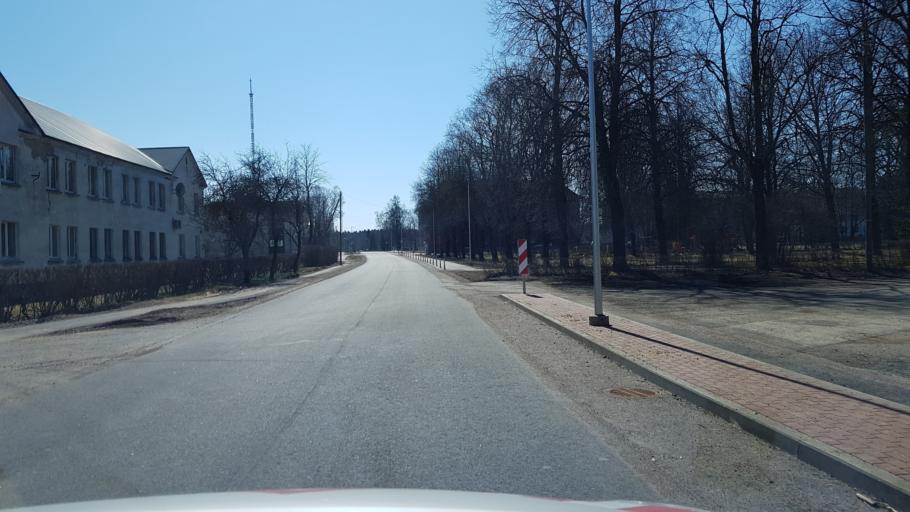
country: EE
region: Ida-Virumaa
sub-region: Kohtla-Nomme vald
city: Kohtla-Nomme
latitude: 59.3568
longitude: 27.1909
